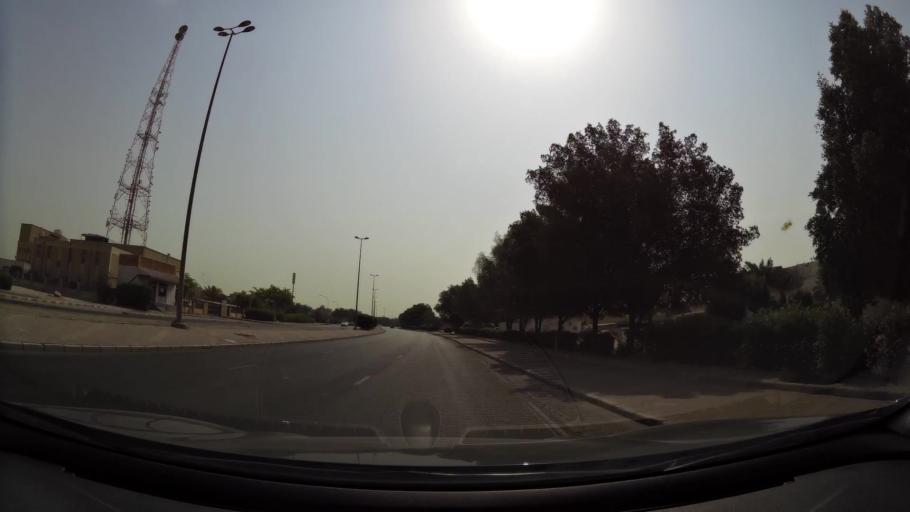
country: KW
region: Al Asimah
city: Ar Rabiyah
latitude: 29.2873
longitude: 47.8811
